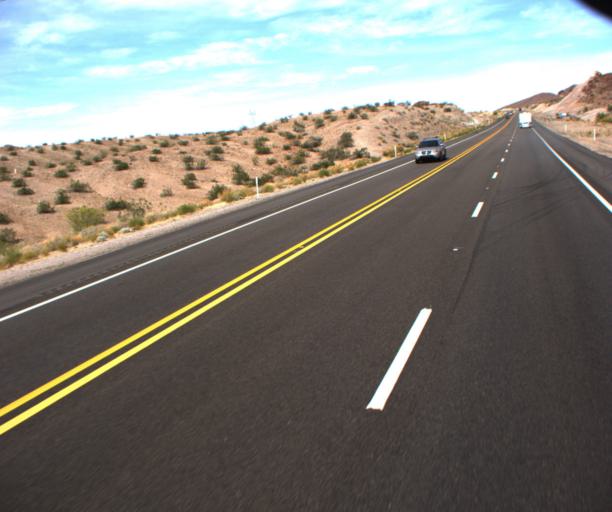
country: US
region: Arizona
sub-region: Mohave County
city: Desert Hills
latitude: 34.6217
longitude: -114.3386
